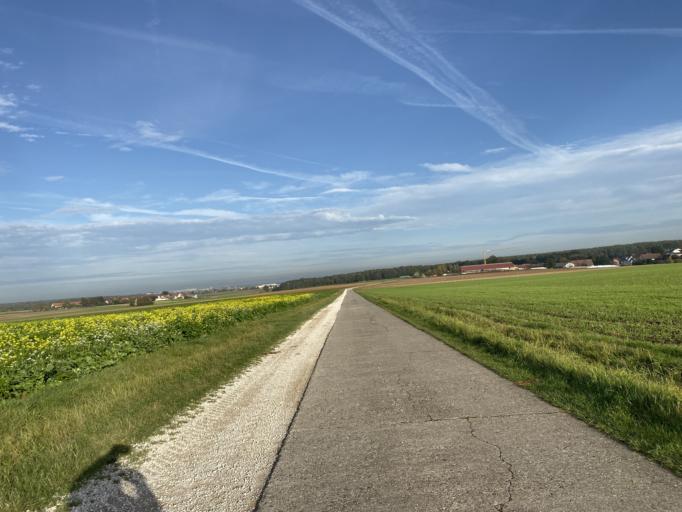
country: DE
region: Bavaria
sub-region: Regierungsbezirk Mittelfranken
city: Puschendorf
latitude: 49.5493
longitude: 10.8306
